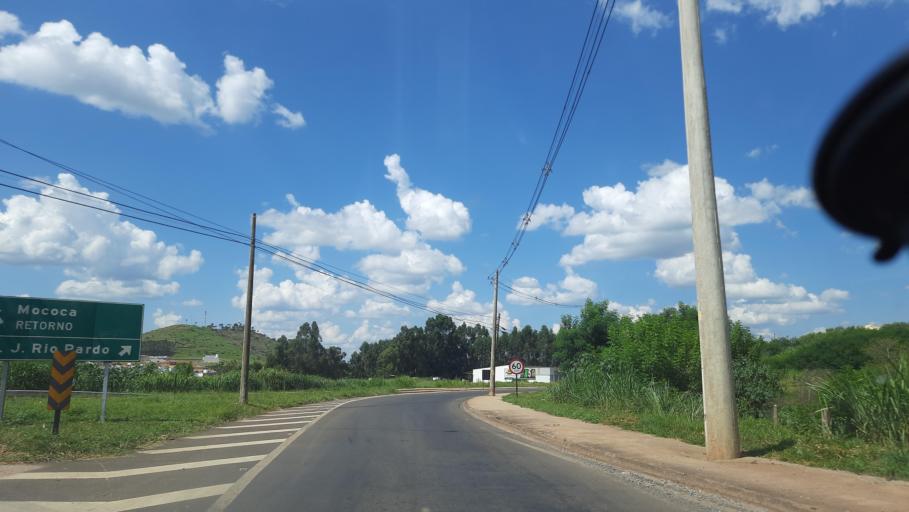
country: BR
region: Sao Paulo
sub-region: Sao Jose Do Rio Pardo
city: Sao Jose do Rio Pardo
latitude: -21.6036
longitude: -46.9152
